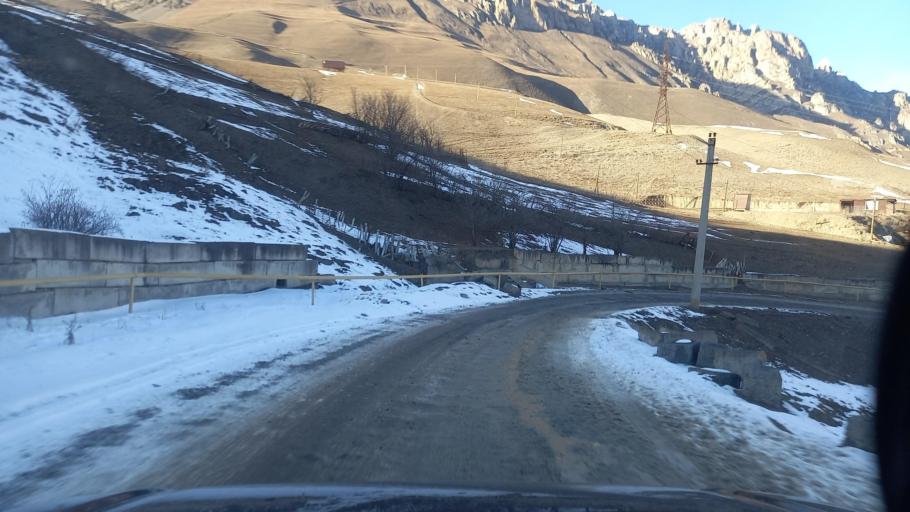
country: RU
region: Ingushetiya
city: Dzhayrakh
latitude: 42.8440
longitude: 44.5080
